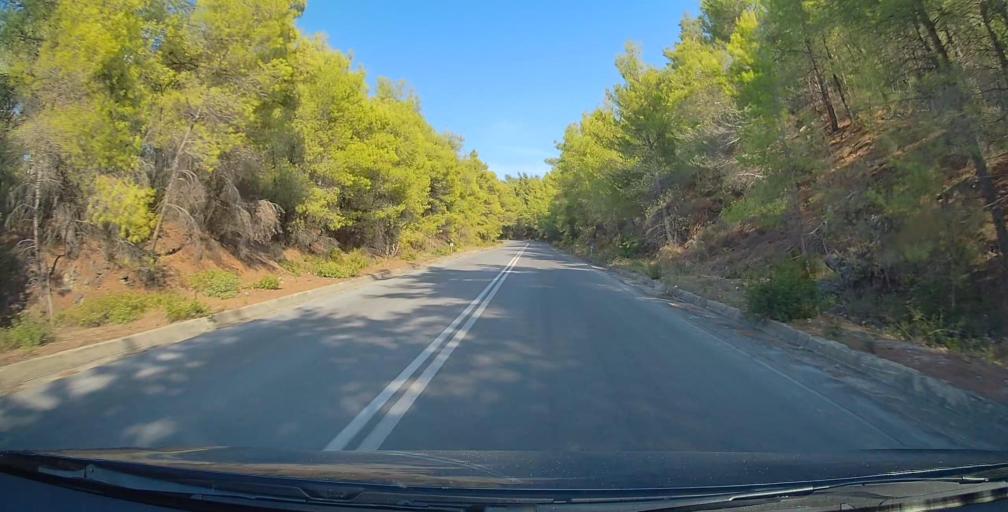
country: GR
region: Central Macedonia
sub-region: Nomos Chalkidikis
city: Neos Marmaras
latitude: 40.0648
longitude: 23.8047
